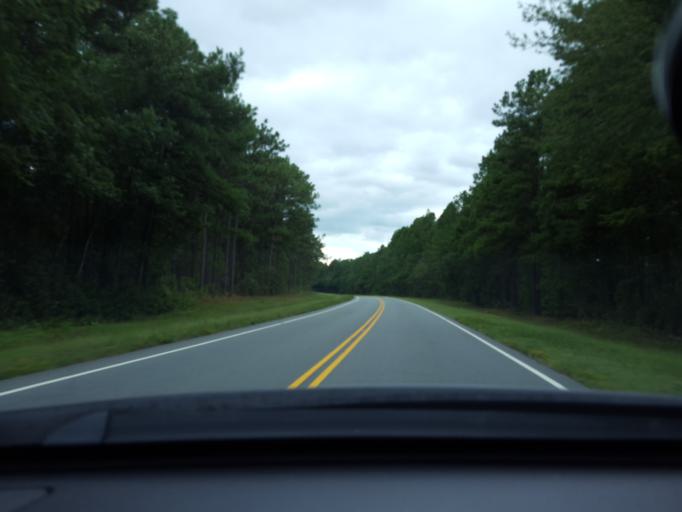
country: US
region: North Carolina
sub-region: Bladen County
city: Elizabethtown
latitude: 34.7035
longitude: -78.4731
